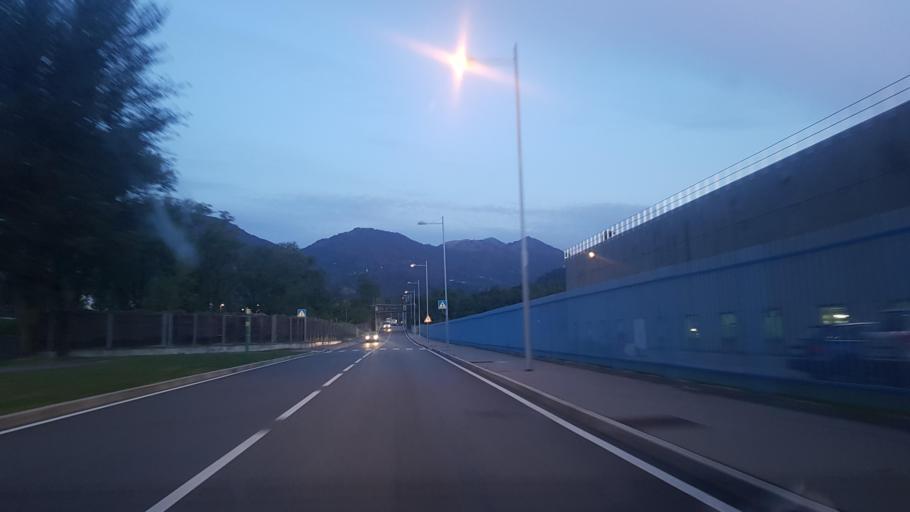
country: IT
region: Friuli Venezia Giulia
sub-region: Provincia di Udine
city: Tolmezzo
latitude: 46.3912
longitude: 13.0252
